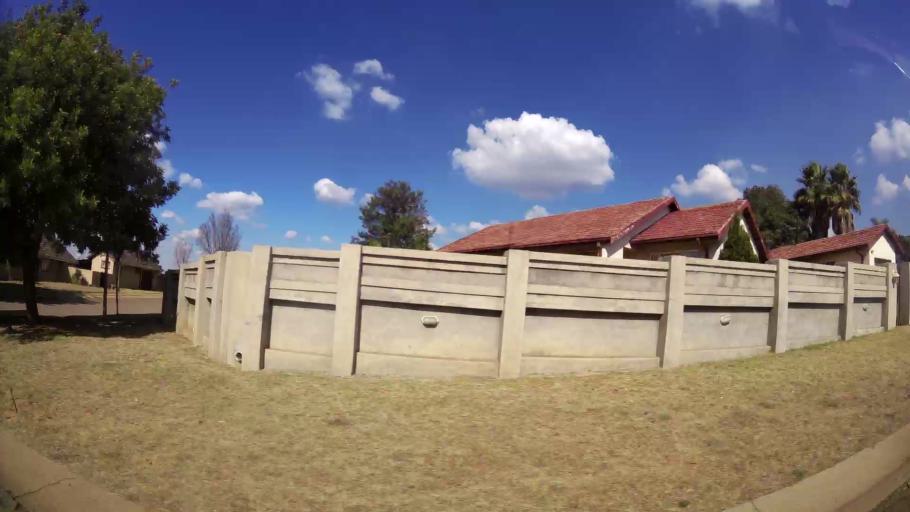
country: ZA
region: Mpumalanga
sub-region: Nkangala District Municipality
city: Witbank
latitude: -25.9370
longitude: 29.2412
